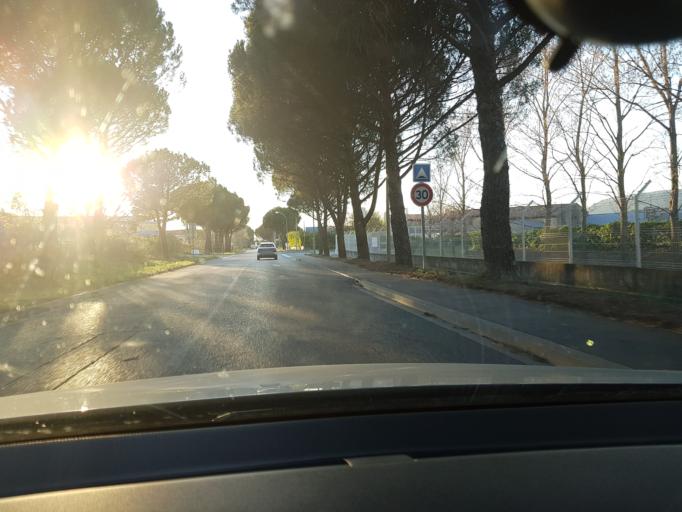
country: FR
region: Provence-Alpes-Cote d'Azur
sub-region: Departement des Bouches-du-Rhone
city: Rousset
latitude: 43.4699
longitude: 5.6039
